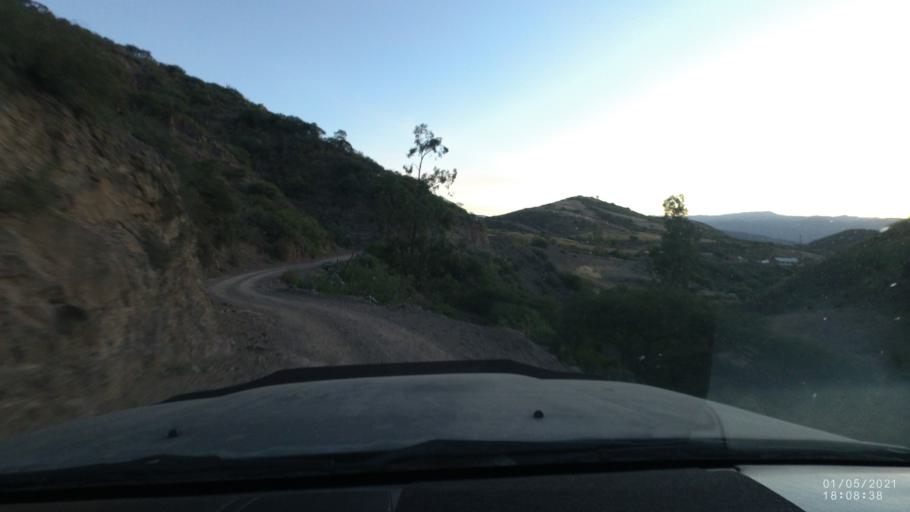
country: BO
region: Cochabamba
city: Capinota
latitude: -17.6857
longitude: -66.1910
